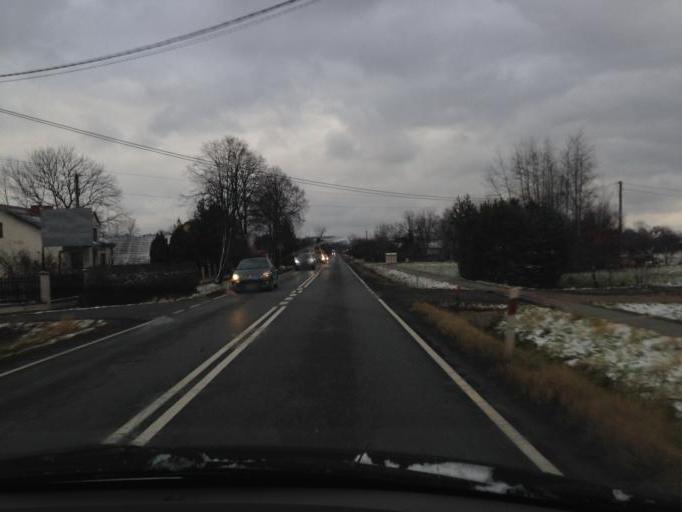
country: PL
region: Lesser Poland Voivodeship
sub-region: Powiat brzeski
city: Czchow
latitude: 49.8539
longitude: 20.6953
